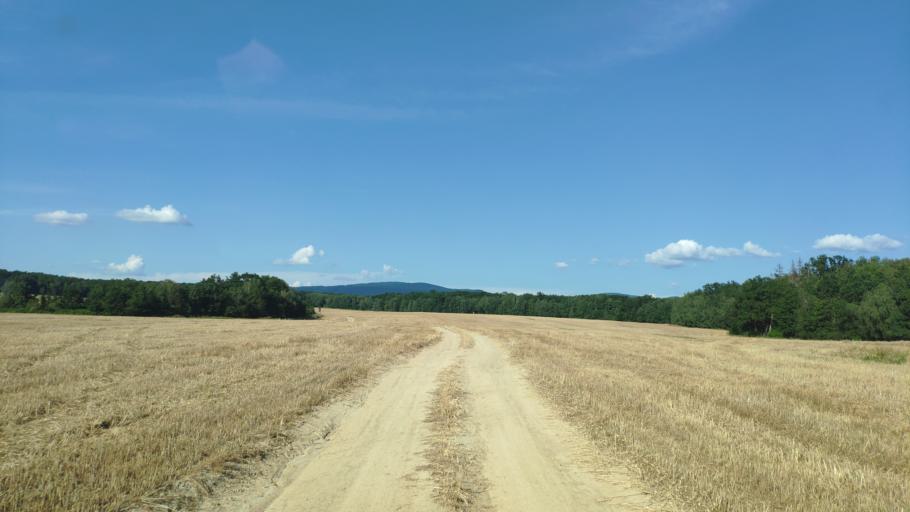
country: SK
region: Presovsky
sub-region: Okres Presov
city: Presov
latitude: 48.9133
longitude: 21.2972
